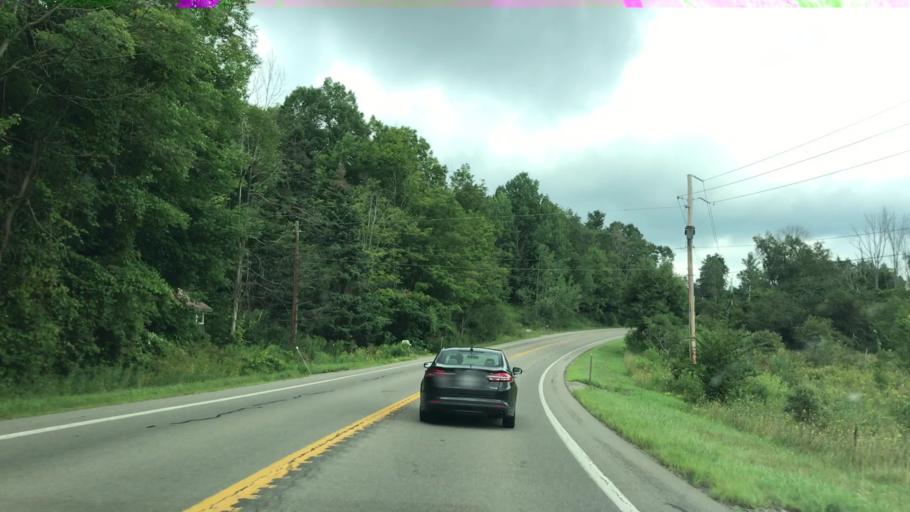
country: US
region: New York
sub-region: Steuben County
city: Bath
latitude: 42.4052
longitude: -77.3515
